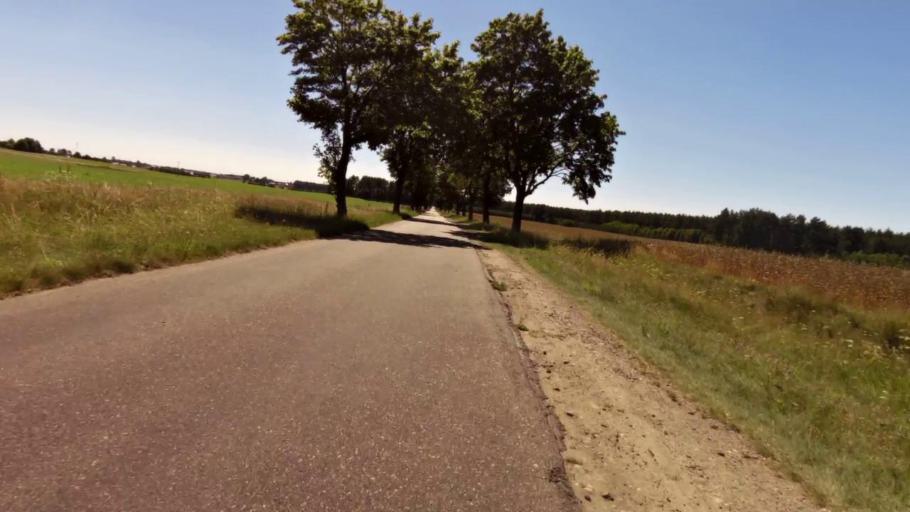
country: PL
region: West Pomeranian Voivodeship
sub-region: Powiat szczecinecki
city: Bialy Bor
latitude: 53.9175
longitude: 16.8394
